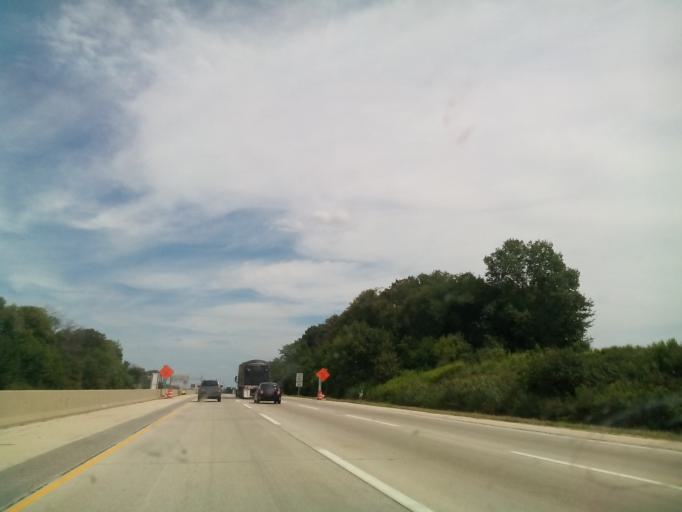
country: US
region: Illinois
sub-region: Kane County
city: North Aurora
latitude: 41.7975
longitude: -88.2978
